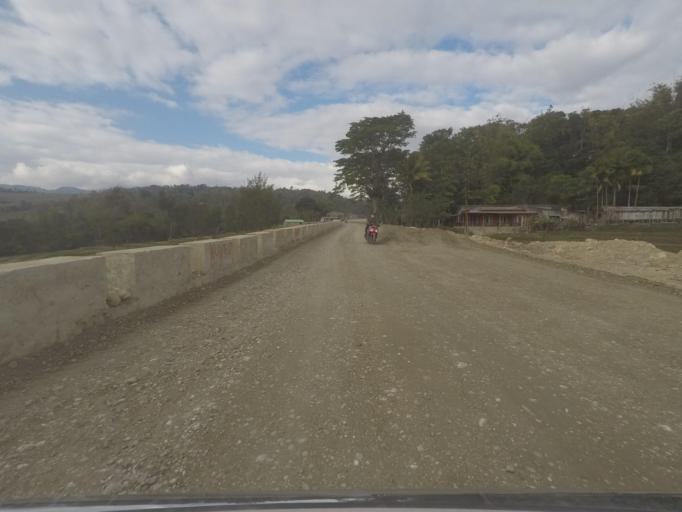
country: TL
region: Baucau
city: Venilale
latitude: -8.6289
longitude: 126.3830
